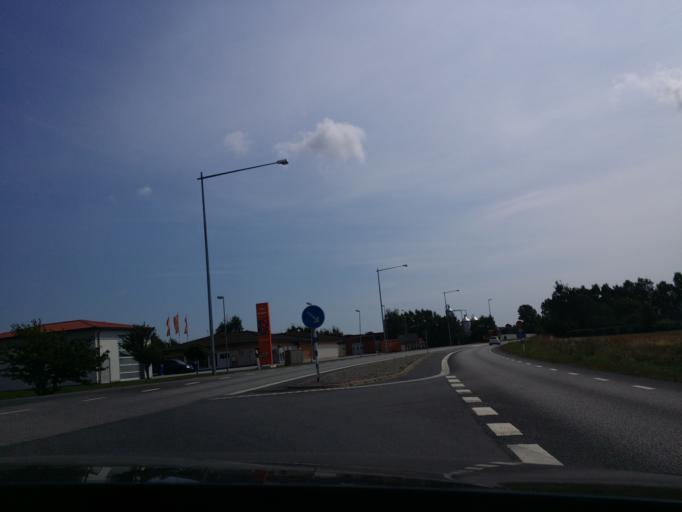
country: SE
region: Blekinge
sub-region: Solvesborgs Kommun
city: Soelvesborg
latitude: 56.0446
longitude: 14.6671
